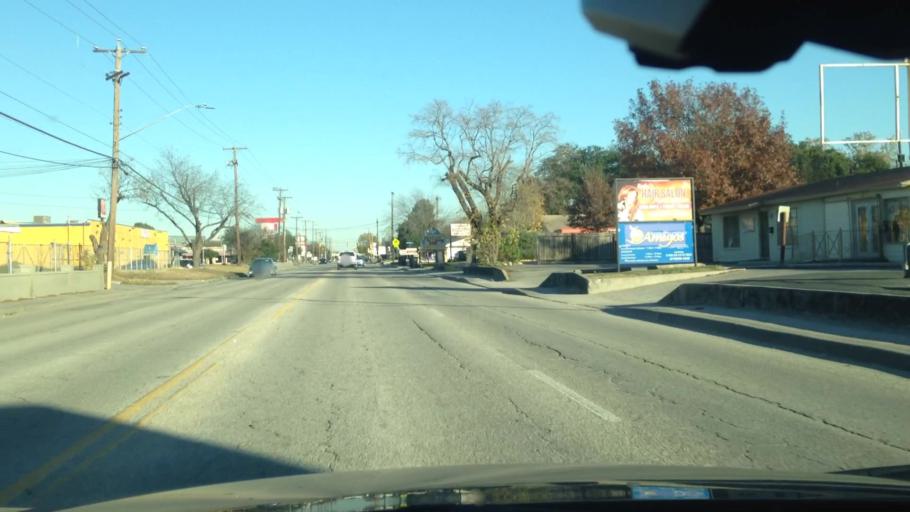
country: US
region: Texas
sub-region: Bexar County
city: Windcrest
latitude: 29.5103
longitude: -98.4058
